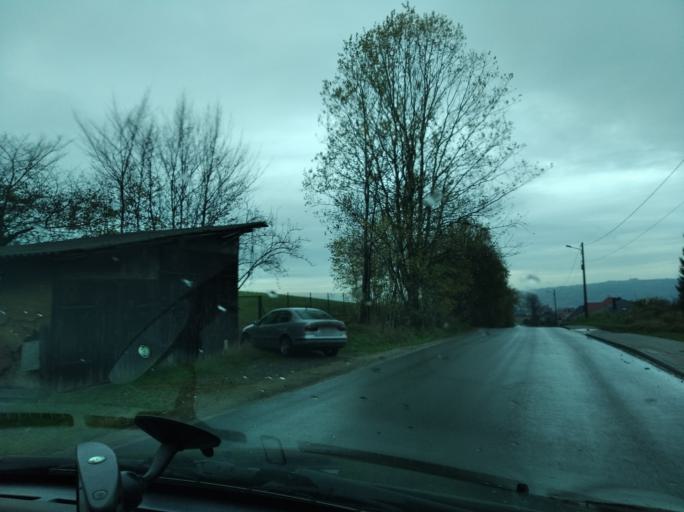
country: PL
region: Subcarpathian Voivodeship
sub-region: Powiat rzeszowski
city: Tyczyn
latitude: 49.9468
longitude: 22.0386
